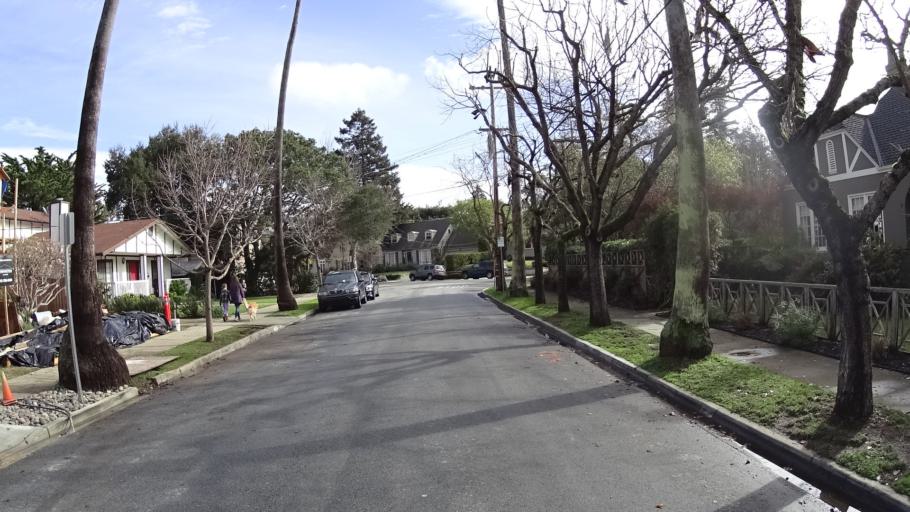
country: US
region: California
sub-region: San Mateo County
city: San Mateo
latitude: 37.5738
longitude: -122.3438
